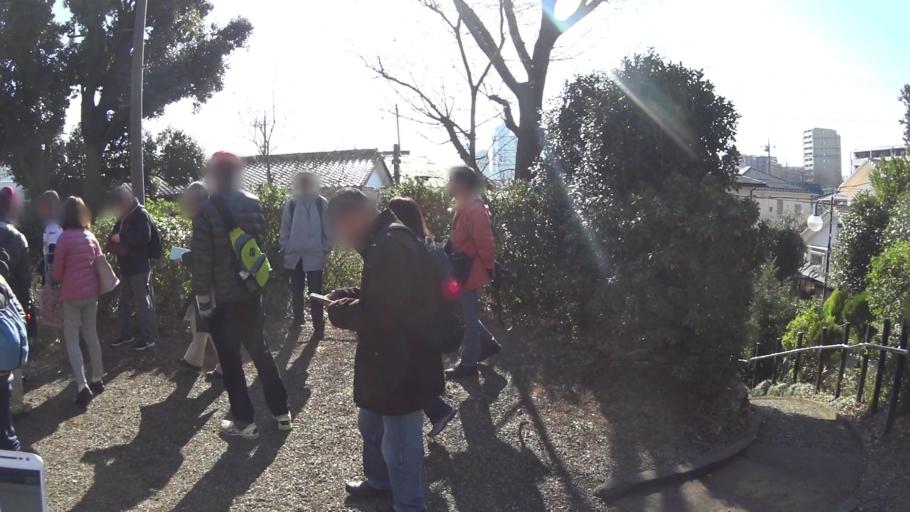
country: JP
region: Saitama
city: Yono
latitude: 35.9029
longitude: 139.6327
